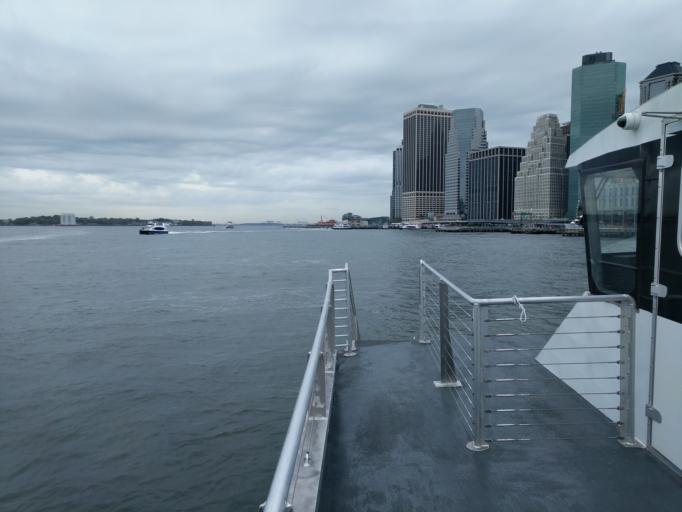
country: US
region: New York
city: New York City
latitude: 40.7048
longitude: -73.9981
